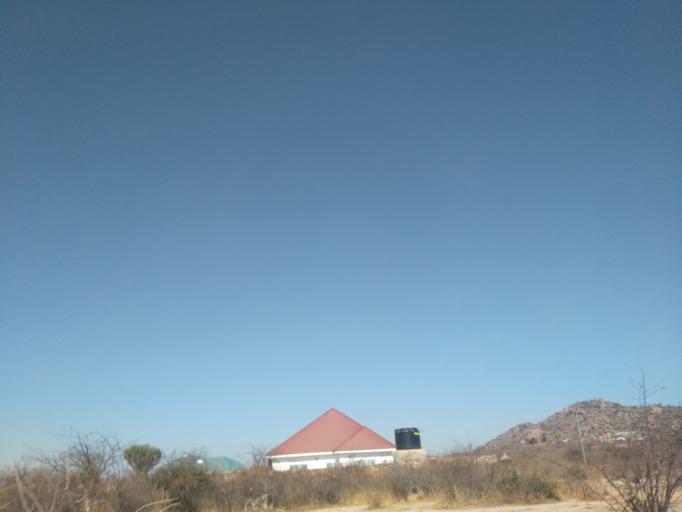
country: TZ
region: Dodoma
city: Dodoma
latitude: -6.1757
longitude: 35.7012
